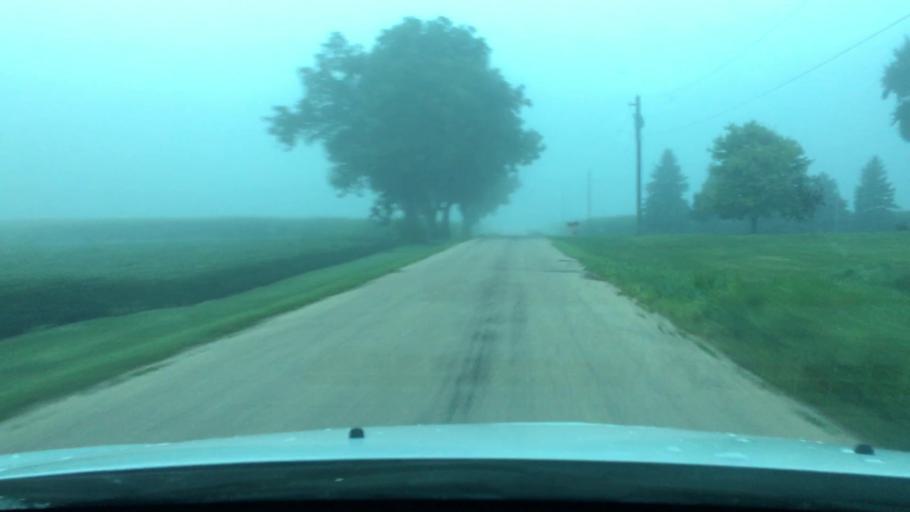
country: US
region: Illinois
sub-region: Ogle County
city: Rochelle
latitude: 41.8681
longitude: -88.9813
